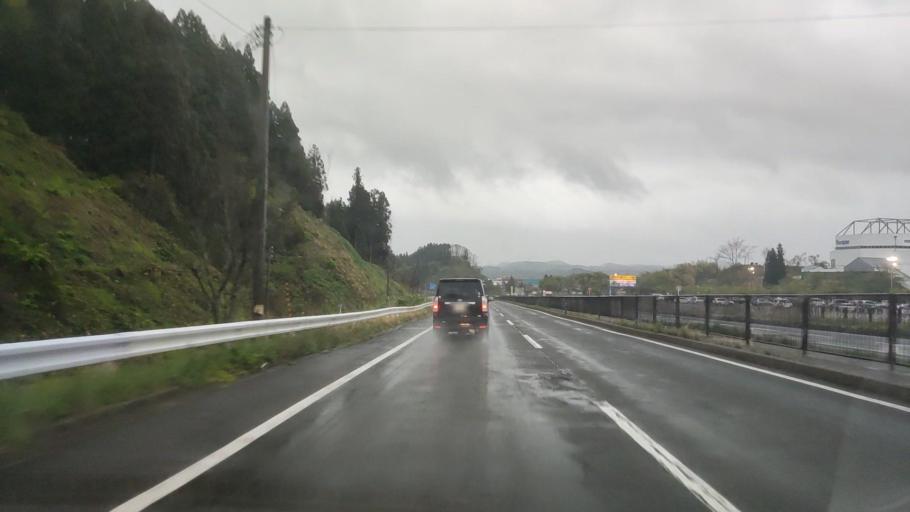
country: JP
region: Akita
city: Akita
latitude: 39.6567
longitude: 140.2027
